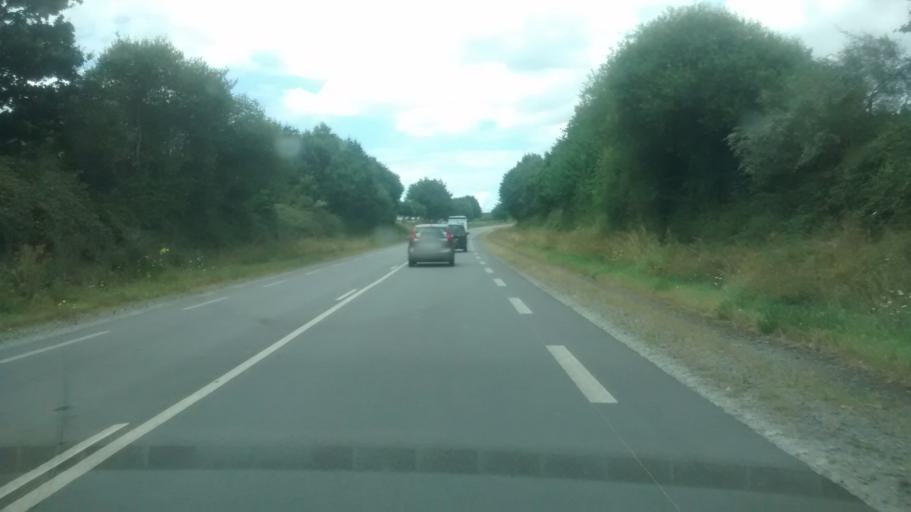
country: FR
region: Brittany
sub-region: Departement du Morbihan
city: Mauron
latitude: 48.0907
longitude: -2.2691
